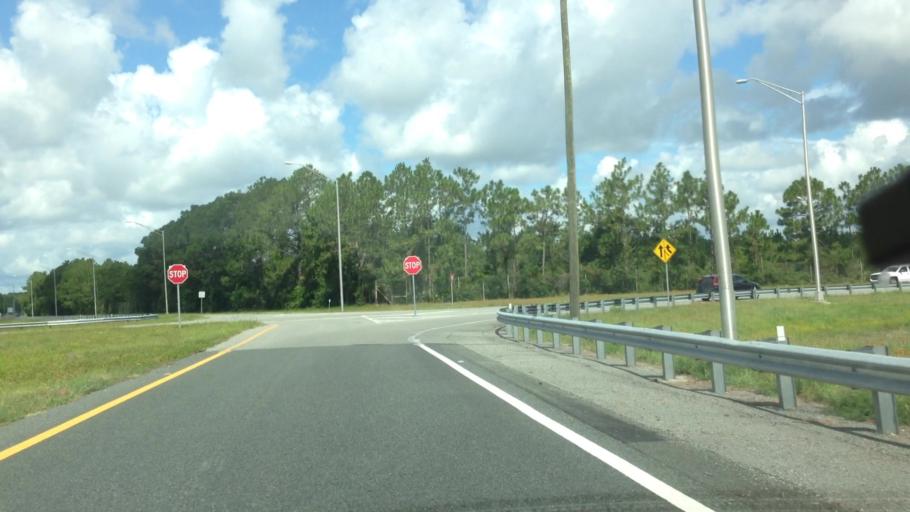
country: US
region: Florida
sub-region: Saint Johns County
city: Ponte Vedra Beach
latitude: 30.2523
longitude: -81.4658
